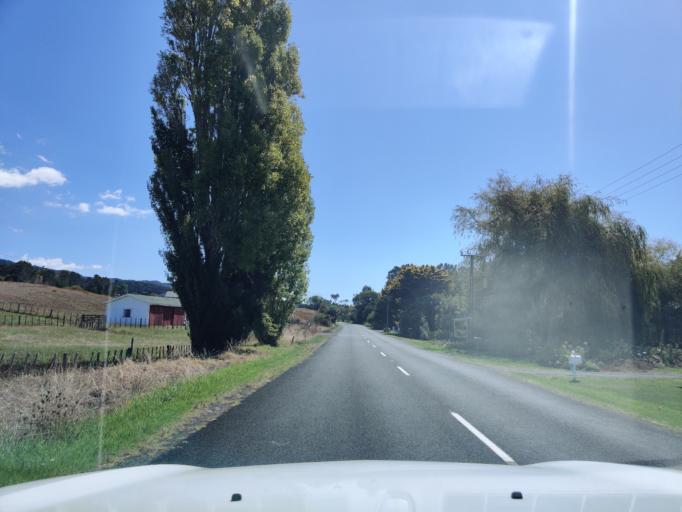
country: NZ
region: Waikato
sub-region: Thames-Coromandel District
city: Thames
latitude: -37.0463
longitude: 175.2984
